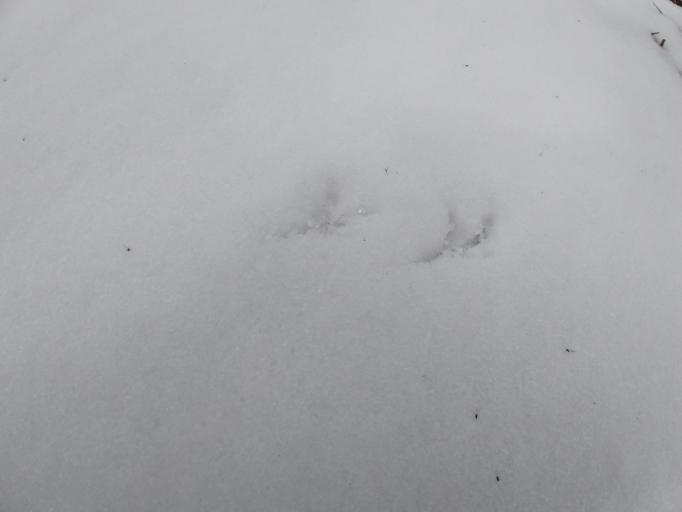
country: IN
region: Himachal Pradesh
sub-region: Kangra
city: Palampur
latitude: 32.1786
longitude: 76.5104
